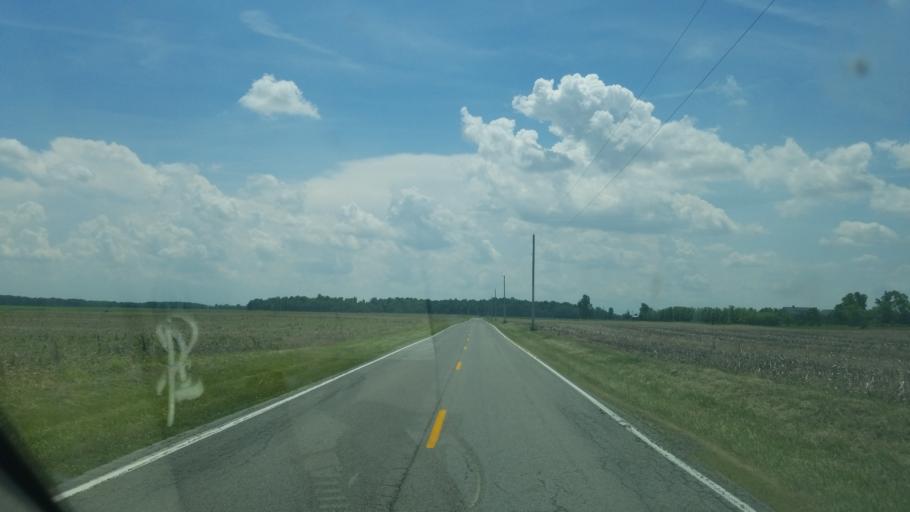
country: US
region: Ohio
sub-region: Hancock County
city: Arlington
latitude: 40.8962
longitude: -83.5948
